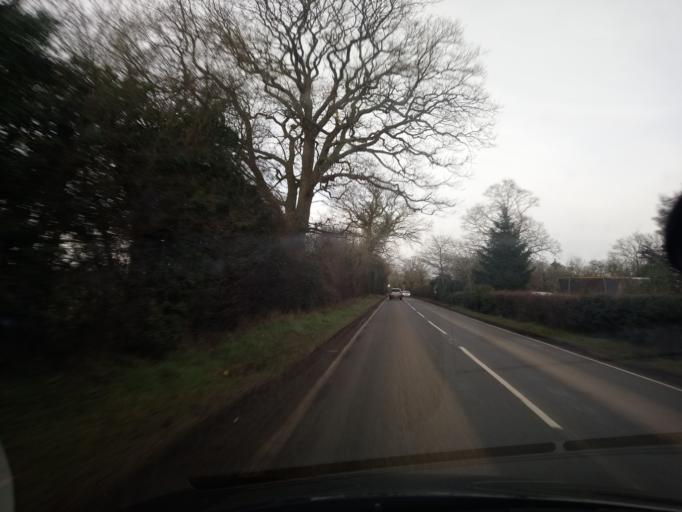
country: GB
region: England
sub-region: Shropshire
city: Prees
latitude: 52.9027
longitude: -2.7041
